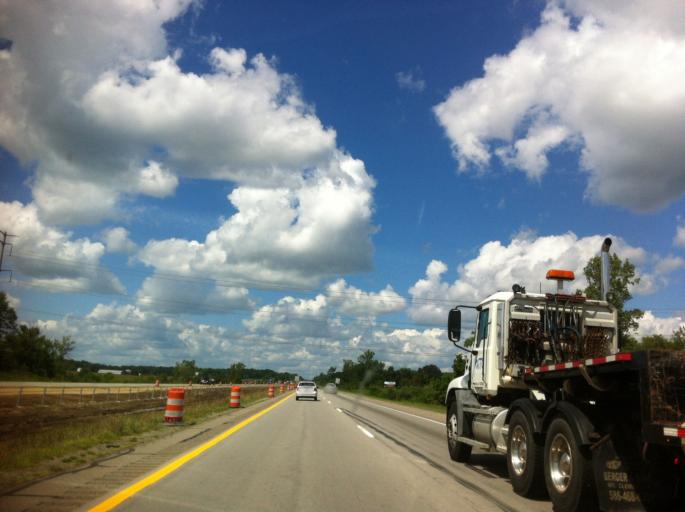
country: US
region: Michigan
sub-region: Washtenaw County
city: Milan
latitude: 42.1185
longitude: -83.6826
